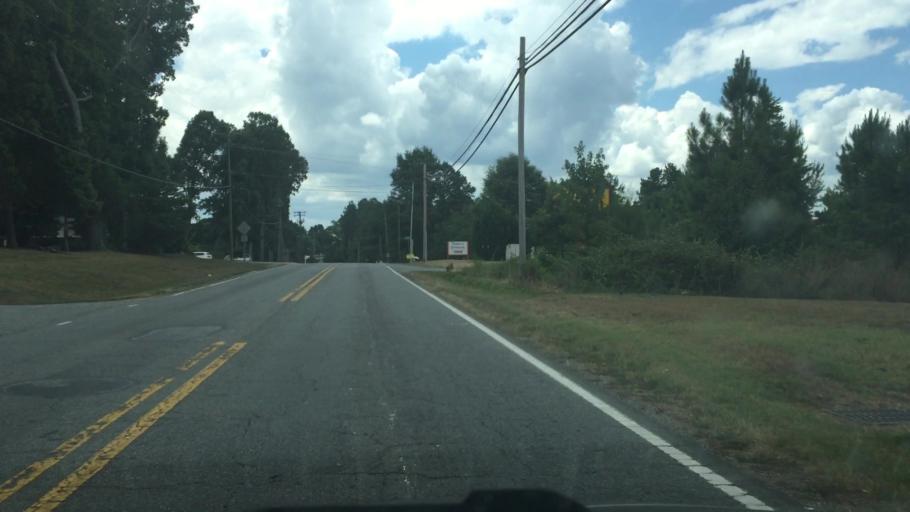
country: US
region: North Carolina
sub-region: Rowan County
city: Enochville
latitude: 35.5158
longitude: -80.6706
